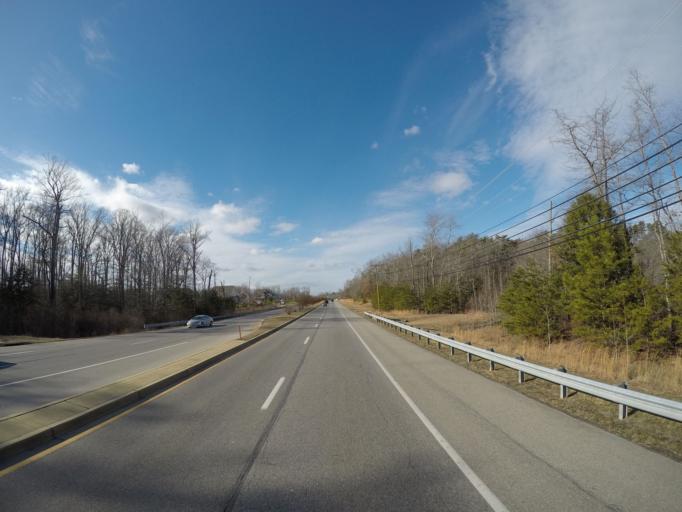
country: US
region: Maryland
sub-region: Charles County
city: Saint Charles
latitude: 38.6009
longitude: -76.9423
